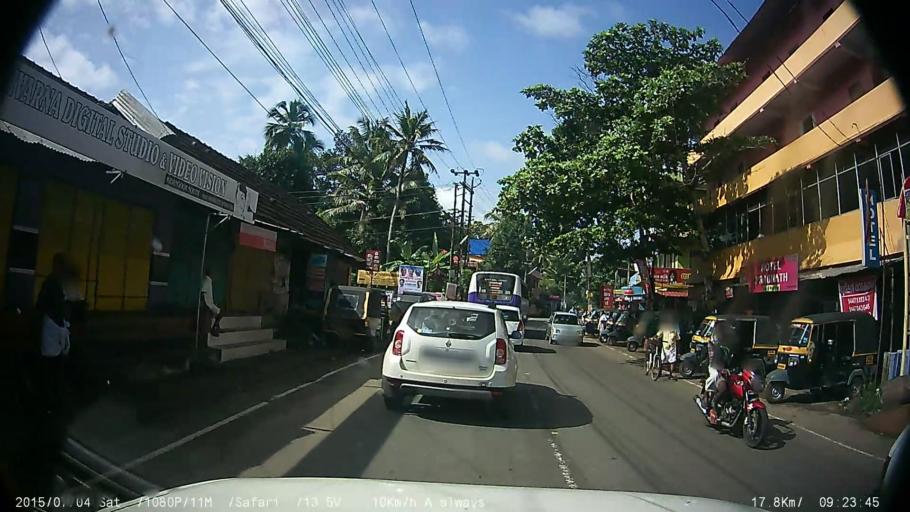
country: IN
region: Kerala
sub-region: Kottayam
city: Palackattumala
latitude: 9.6725
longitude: 76.6108
